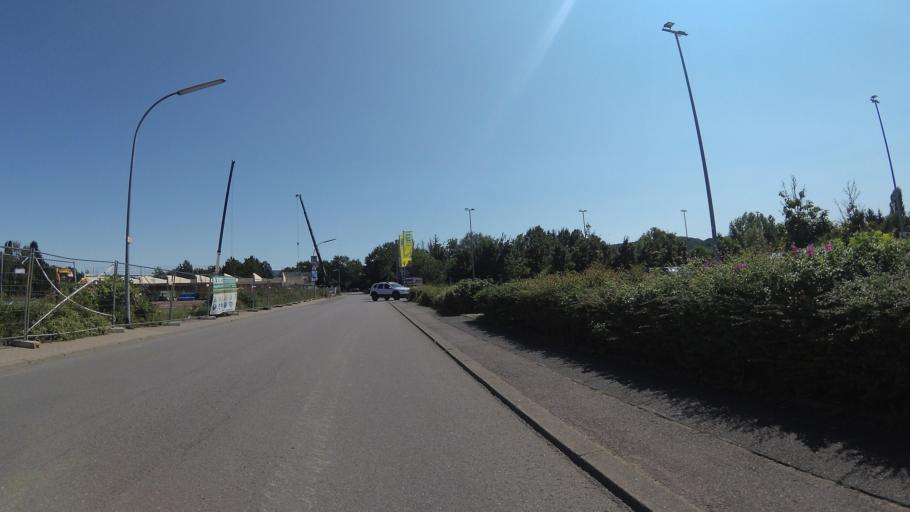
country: DE
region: Saarland
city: Saarbrucken
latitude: 49.2189
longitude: 6.9673
